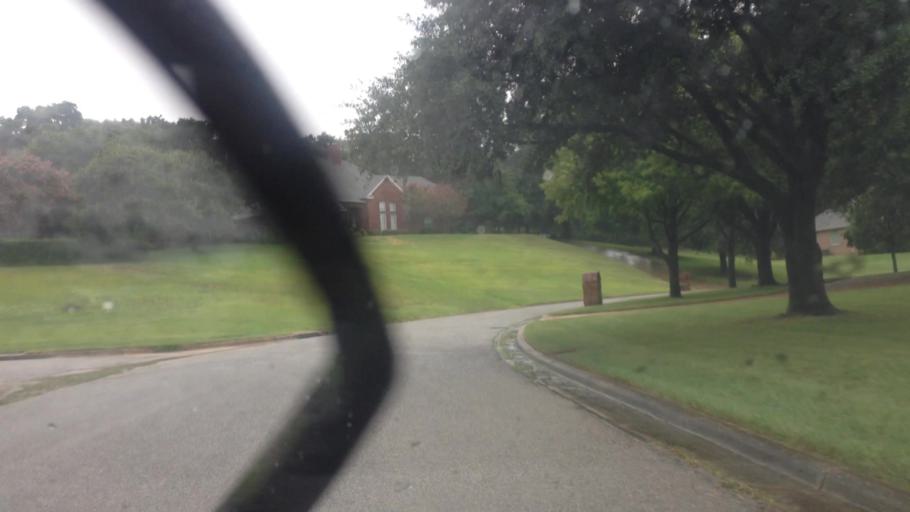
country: US
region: Texas
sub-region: Denton County
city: Trophy Club
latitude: 32.9511
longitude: -97.1965
